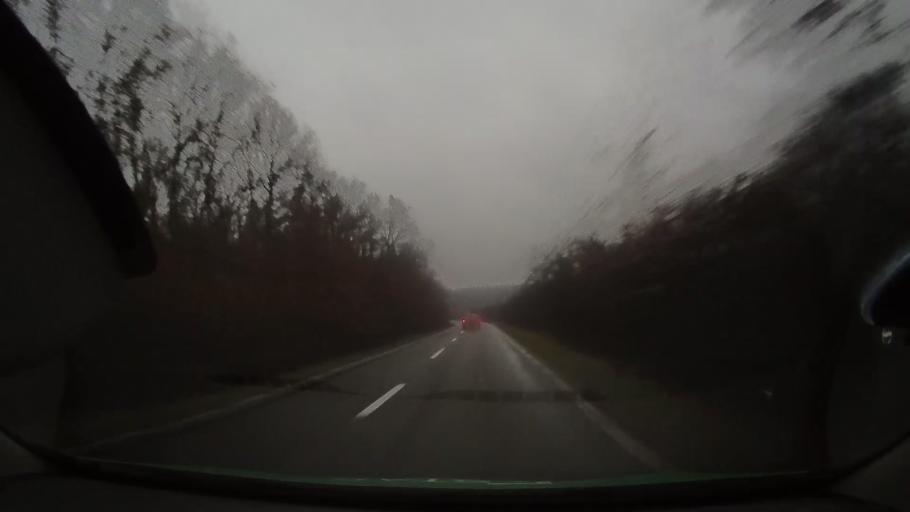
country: RO
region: Arad
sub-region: Comuna Beliu
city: Beliu
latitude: 46.5281
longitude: 21.9544
